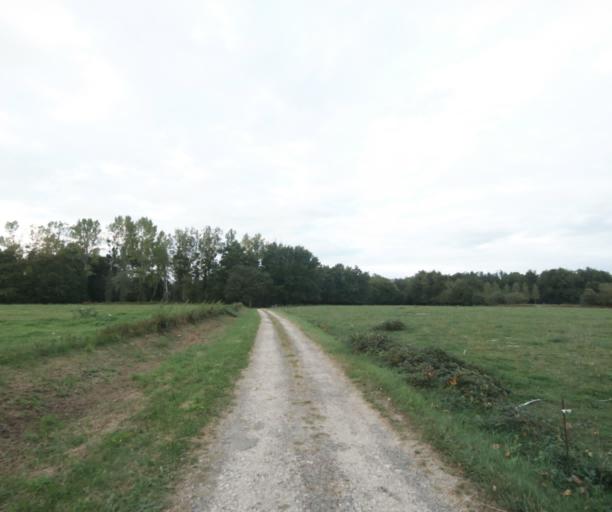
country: FR
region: Aquitaine
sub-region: Departement des Landes
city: Gabarret
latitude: 43.9805
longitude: 0.1036
